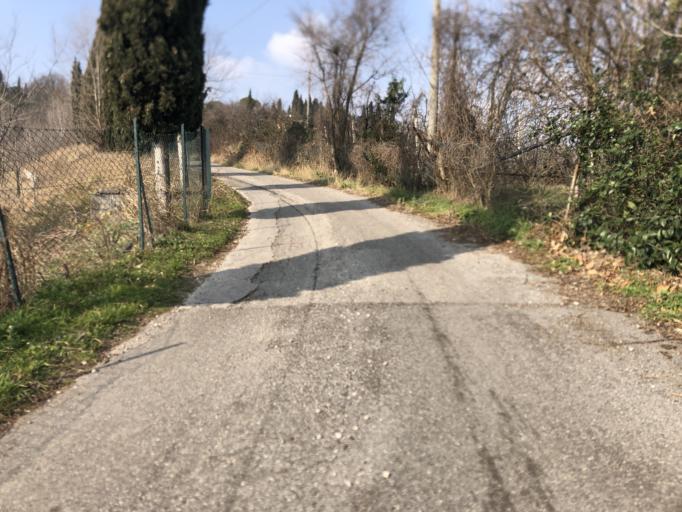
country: IT
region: Veneto
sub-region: Provincia di Verona
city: Sona
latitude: 45.4265
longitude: 10.8420
